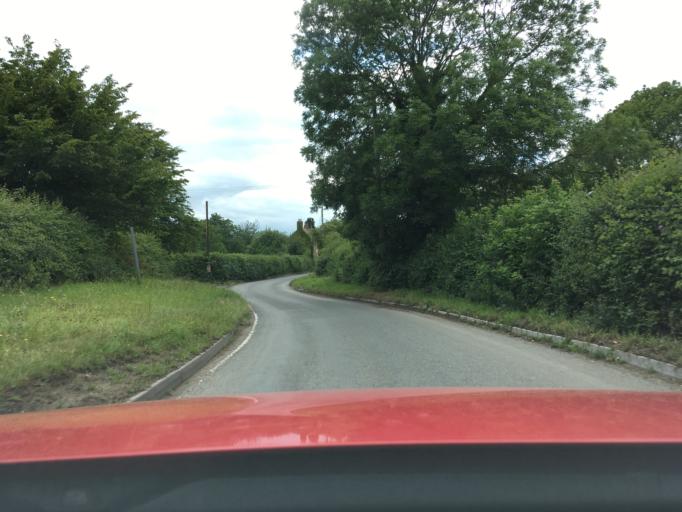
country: GB
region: England
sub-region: Gloucestershire
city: Cinderford
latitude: 51.7960
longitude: -2.4202
